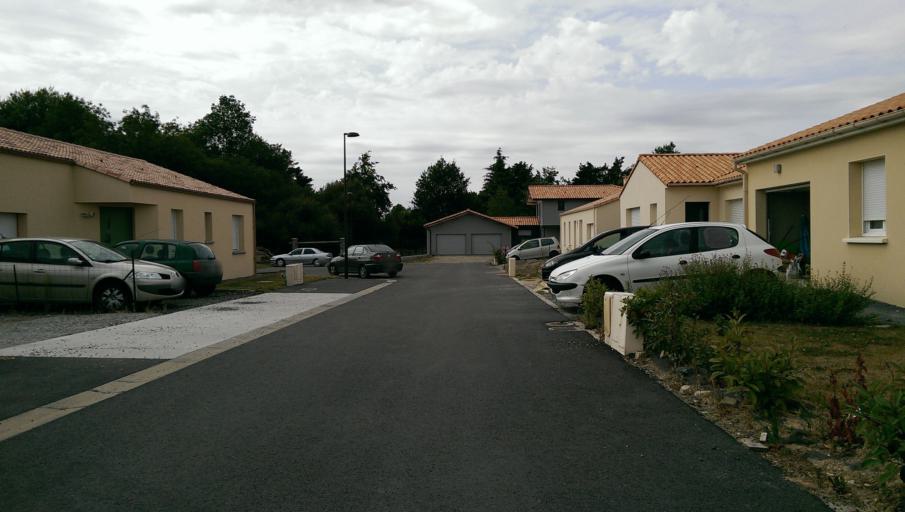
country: FR
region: Pays de la Loire
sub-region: Departement de la Loire-Atlantique
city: La Planche
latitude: 47.0126
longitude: -1.4304
